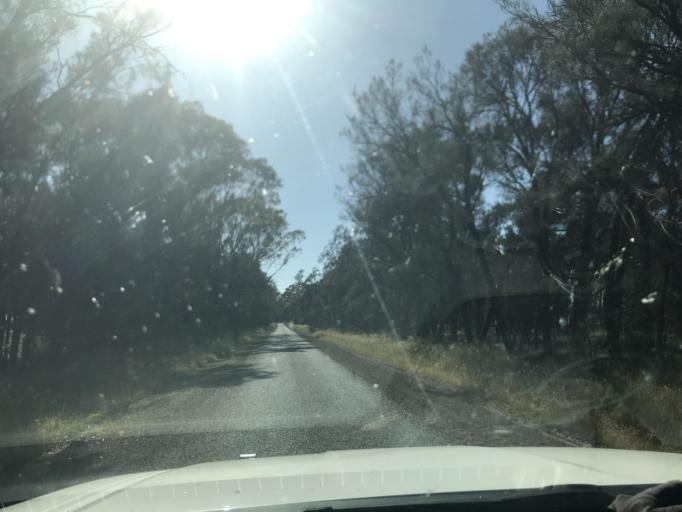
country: AU
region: Victoria
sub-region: Horsham
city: Horsham
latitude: -37.0118
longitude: 141.6655
